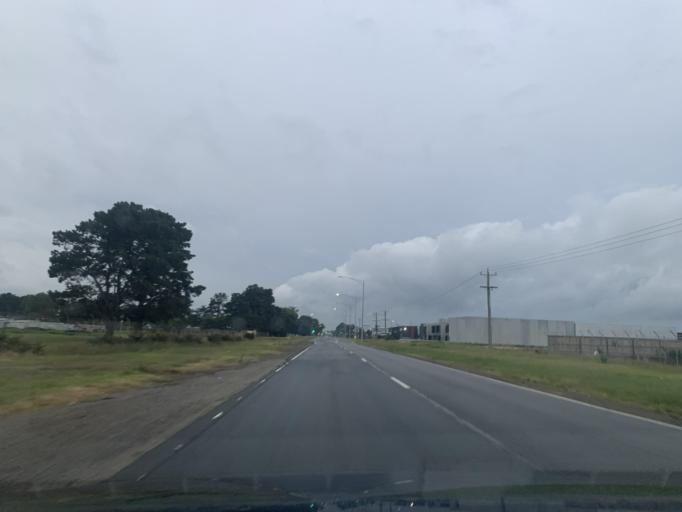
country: AU
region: Victoria
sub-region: Greater Dandenong
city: Keysborough
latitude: -38.0293
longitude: 145.1825
